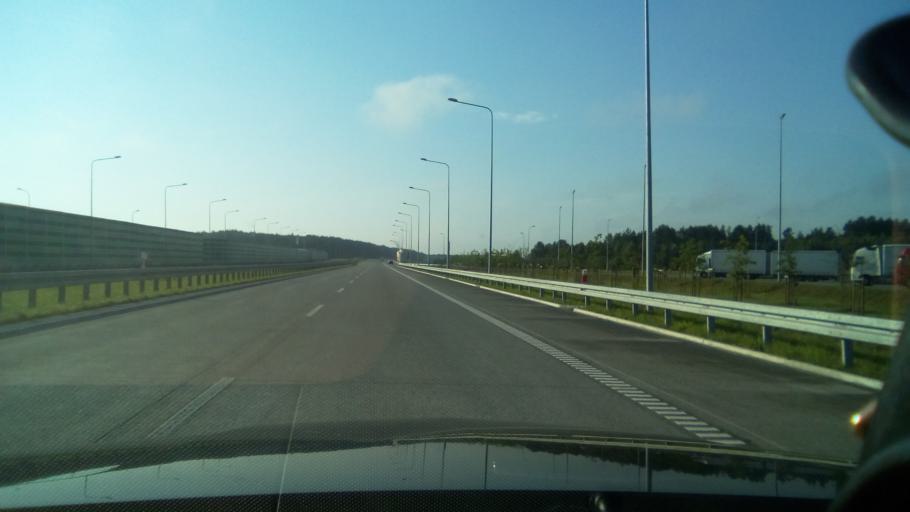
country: PL
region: Silesian Voivodeship
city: Wozniki
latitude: 50.5758
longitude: 19.0500
